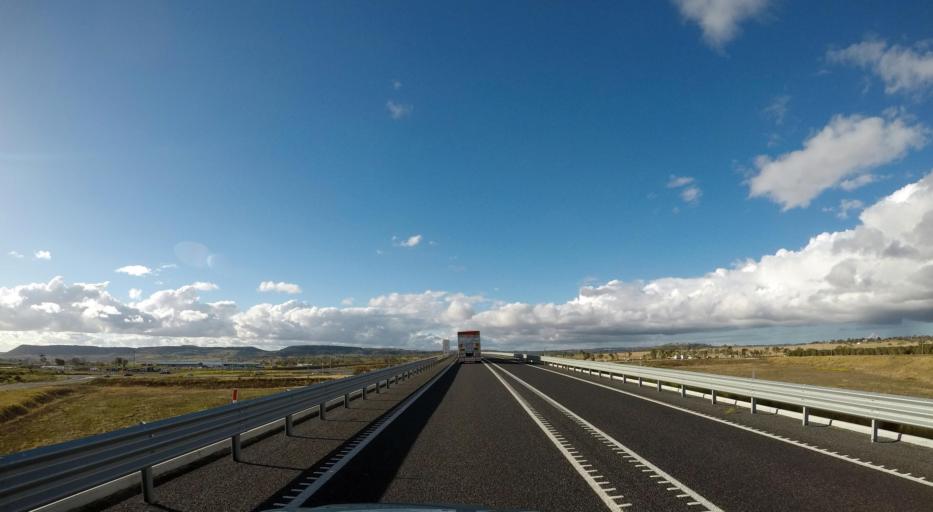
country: AU
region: Queensland
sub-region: Toowoomba
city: Wilsonton Heights
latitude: -27.5263
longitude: 151.8597
